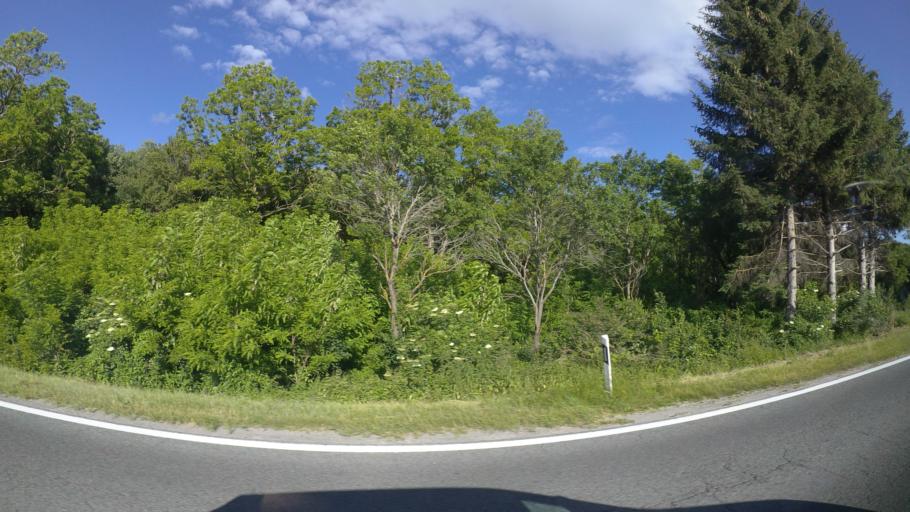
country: BA
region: Federation of Bosnia and Herzegovina
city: Bihac
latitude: 44.6075
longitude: 15.7366
